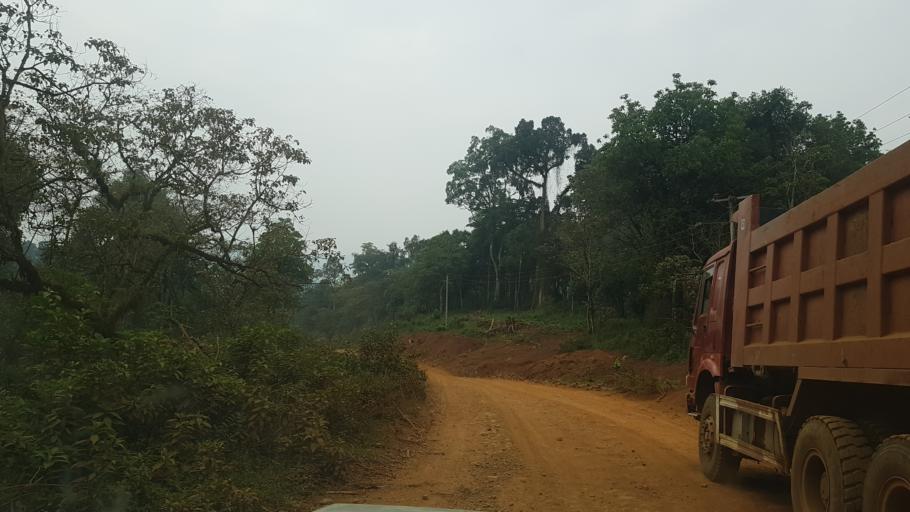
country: ET
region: Oromiya
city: Gore
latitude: 7.8826
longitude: 35.4849
